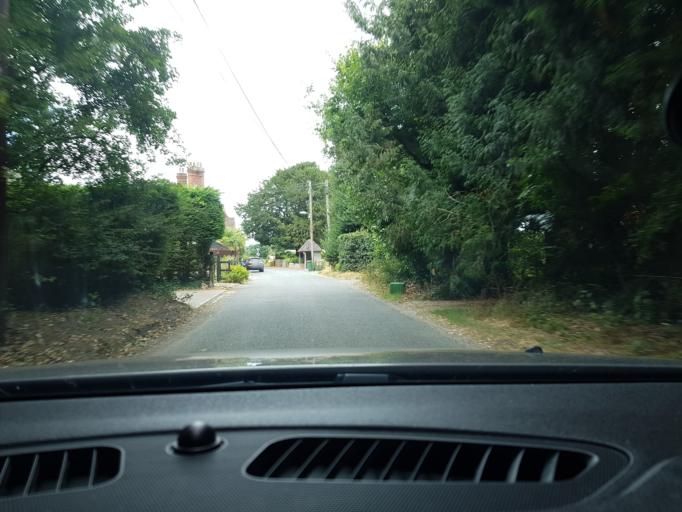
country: GB
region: England
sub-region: West Berkshire
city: Hungerford
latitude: 51.4409
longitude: -1.4876
